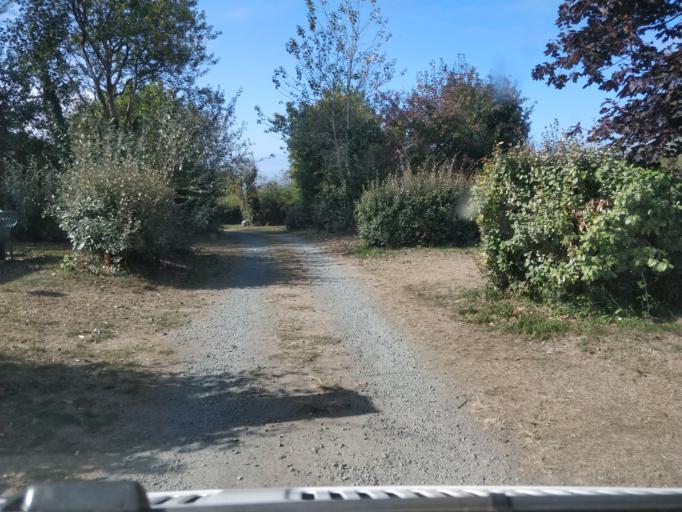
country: FR
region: Brittany
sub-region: Departement du Finistere
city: Plouhinec
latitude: 48.0067
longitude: -4.4942
